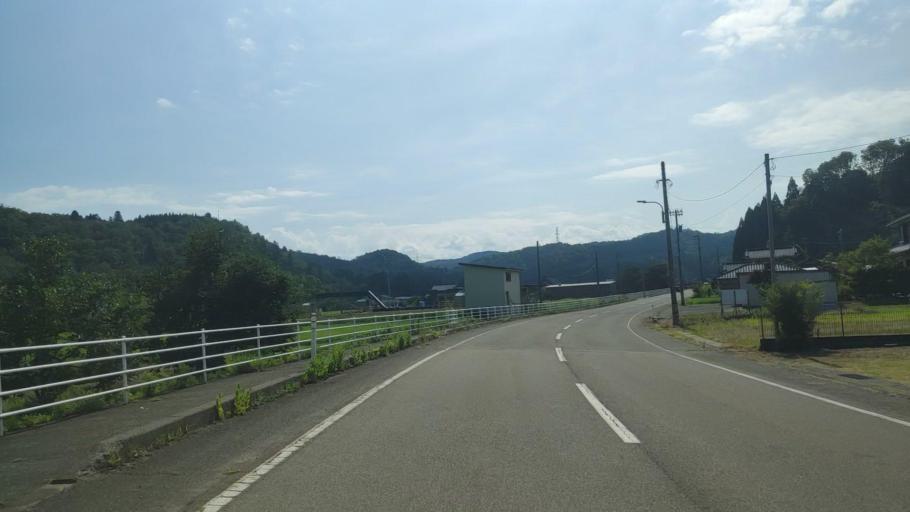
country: JP
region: Ishikawa
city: Komatsu
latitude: 36.3582
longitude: 136.4999
